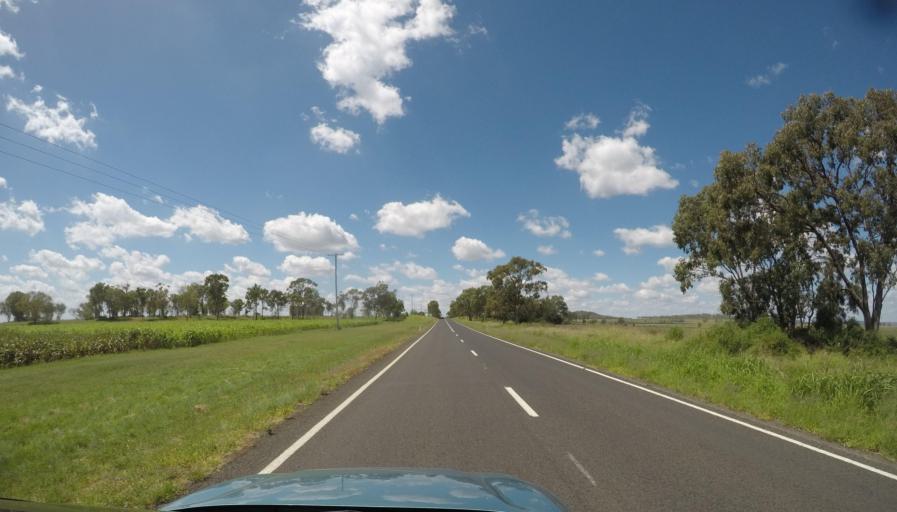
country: AU
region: Queensland
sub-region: Toowoomba
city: Oakey
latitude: -27.5311
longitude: 151.6085
